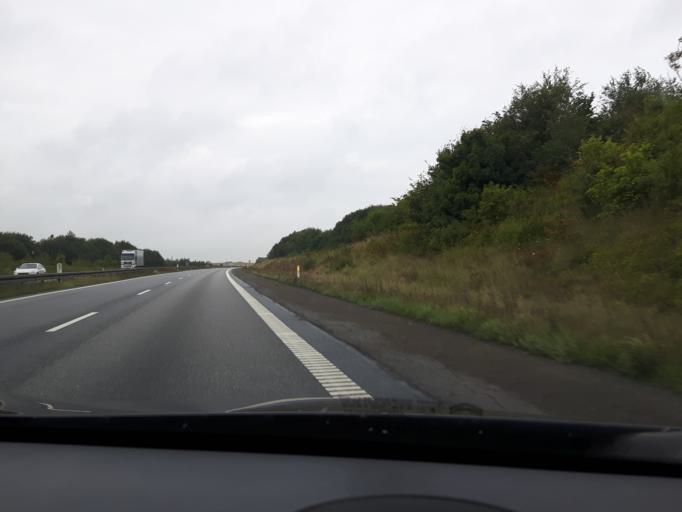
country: DK
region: North Denmark
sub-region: Mariagerfjord Kommune
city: Hobro
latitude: 56.5902
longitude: 9.7719
